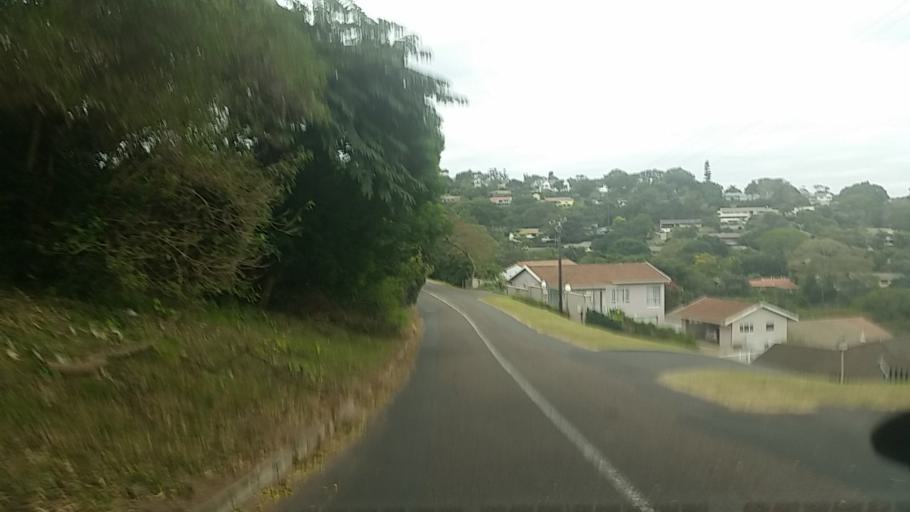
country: ZA
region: KwaZulu-Natal
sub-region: eThekwini Metropolitan Municipality
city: Berea
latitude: -29.8427
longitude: 30.9330
